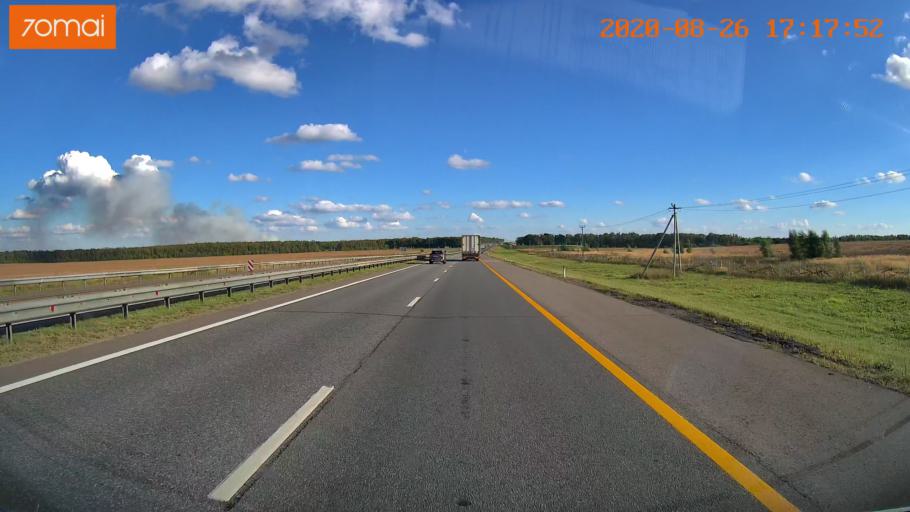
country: RU
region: Tula
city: Volovo
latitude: 53.6178
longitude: 38.0918
